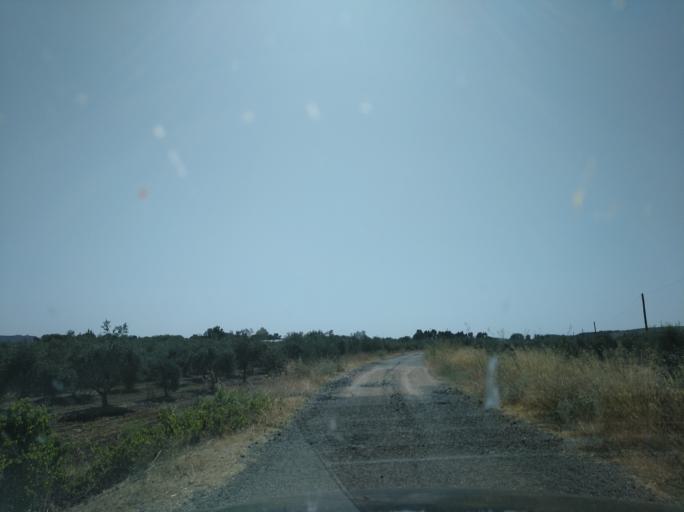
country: PT
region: Portalegre
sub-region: Campo Maior
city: Campo Maior
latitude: 39.0760
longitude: -7.0189
